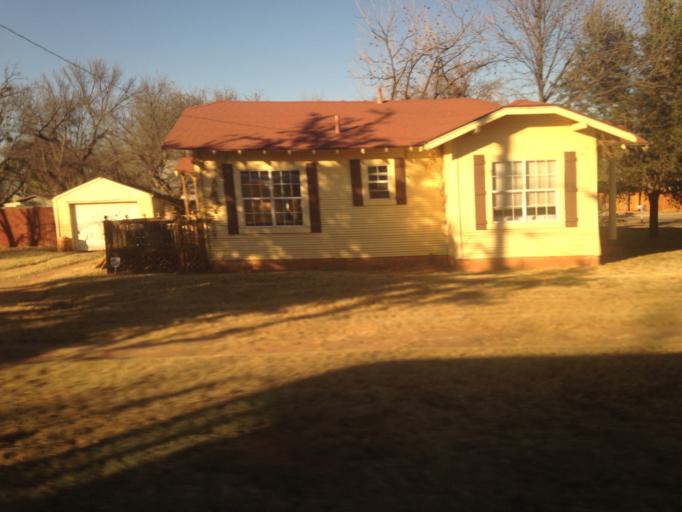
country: US
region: Texas
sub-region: Taylor County
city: Abilene
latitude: 32.4438
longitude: -99.7604
